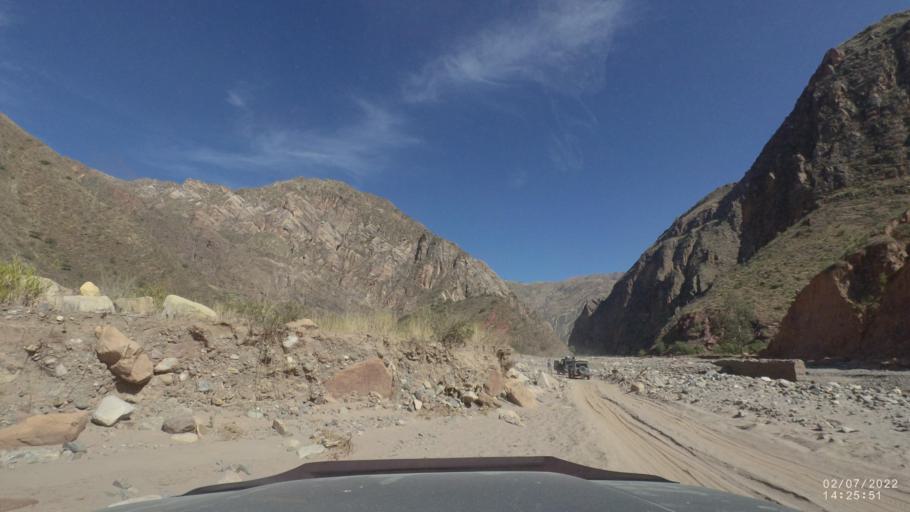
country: BO
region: Cochabamba
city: Irpa Irpa
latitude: -17.8349
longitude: -66.4146
